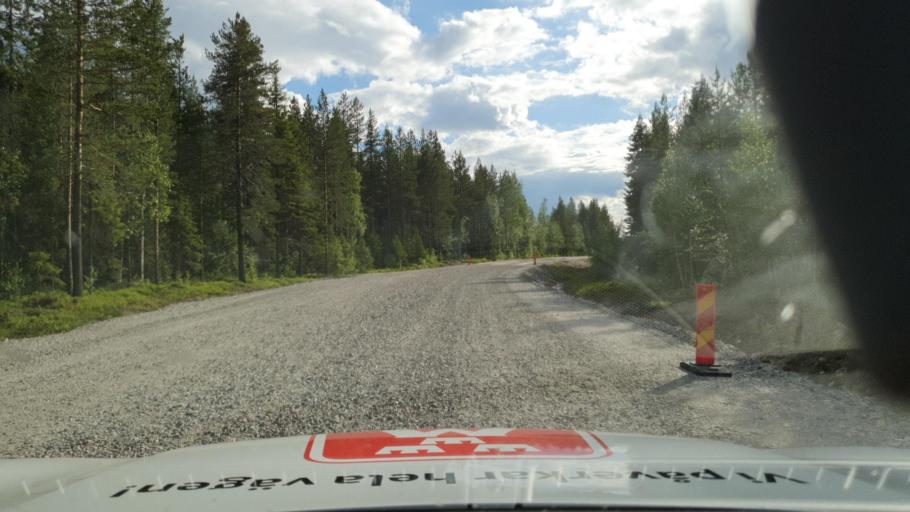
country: SE
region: Vaesterbotten
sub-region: Vindelns Kommun
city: Vindeln
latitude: 64.4346
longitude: 19.7183
